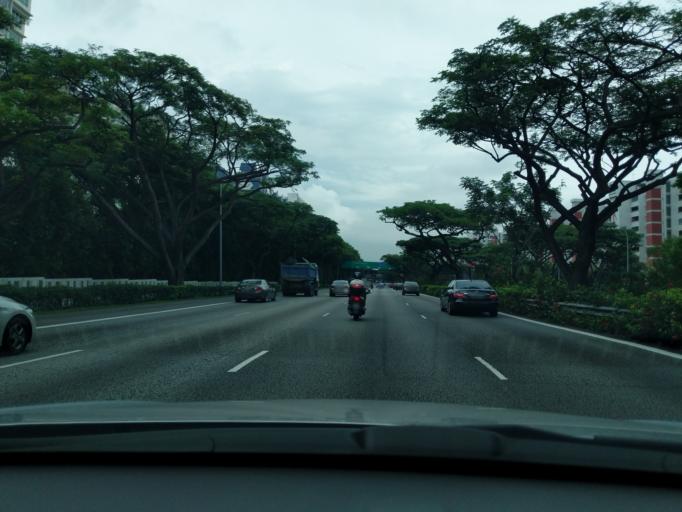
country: SG
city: Singapore
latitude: 1.3302
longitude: 103.9151
